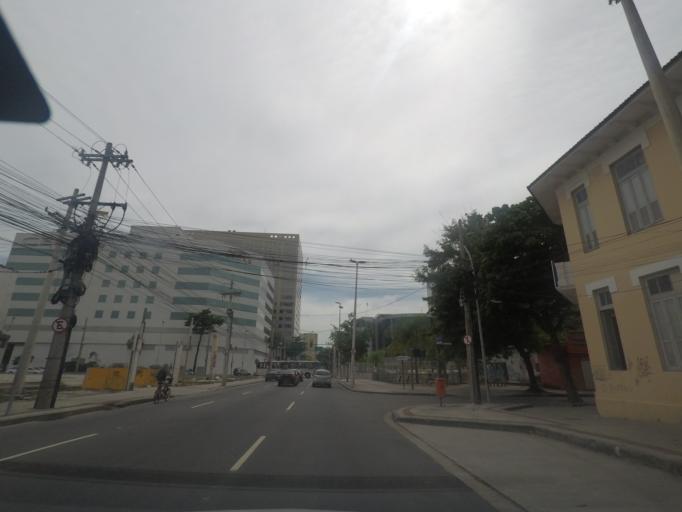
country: BR
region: Rio de Janeiro
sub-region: Rio De Janeiro
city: Rio de Janeiro
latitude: -22.9095
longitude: -43.2011
